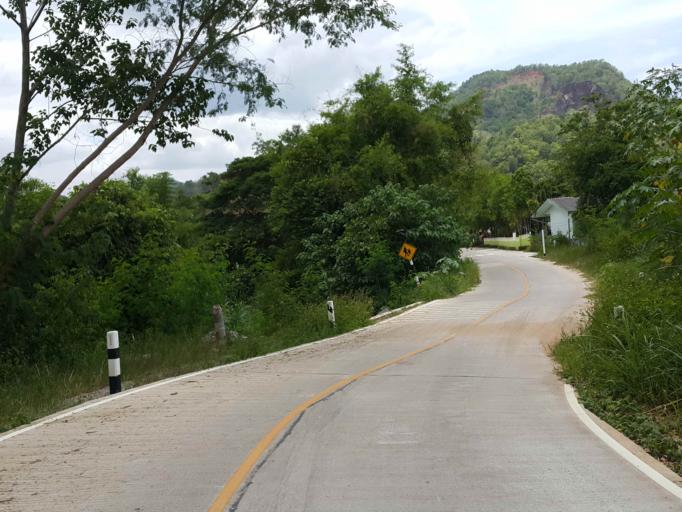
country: TH
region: Chiang Mai
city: Hang Dong
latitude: 18.7629
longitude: 98.8751
